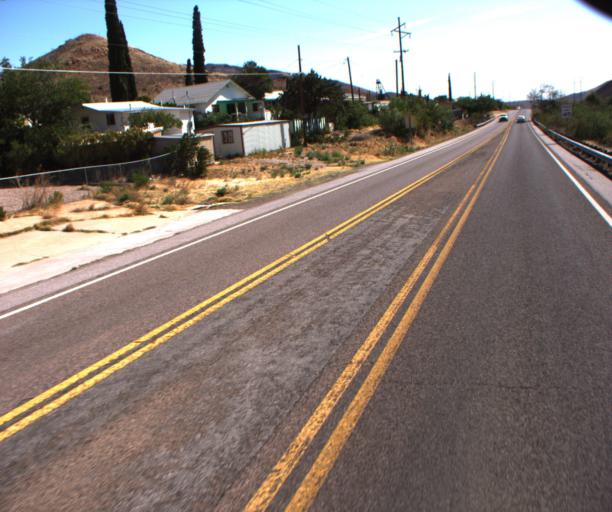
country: US
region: Arizona
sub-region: Cochise County
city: Bisbee
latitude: 31.4273
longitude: -109.8859
